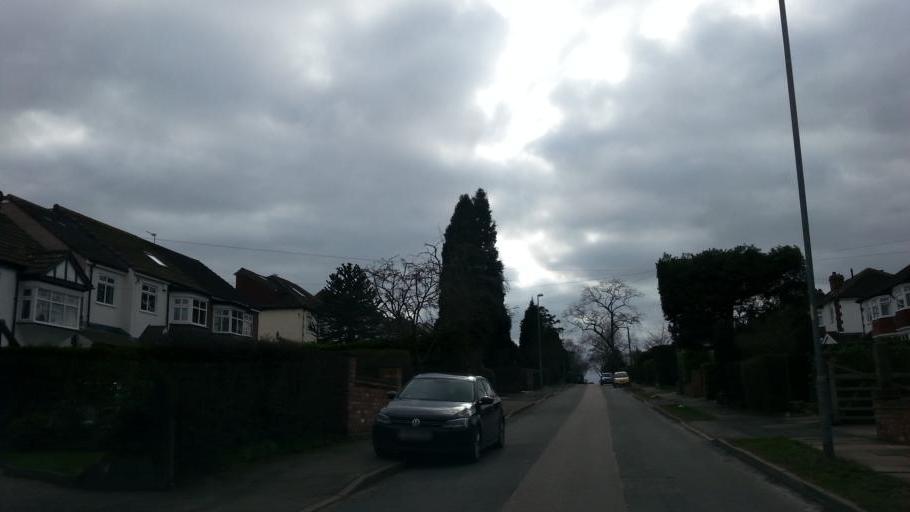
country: GB
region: England
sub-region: Walsall
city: Streetly
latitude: 52.5792
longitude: -1.8803
